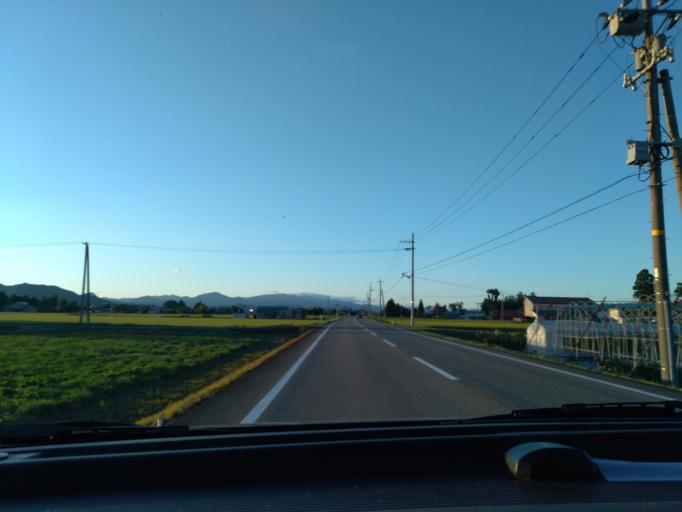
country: JP
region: Akita
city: Kakunodatemachi
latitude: 39.5117
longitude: 140.5589
